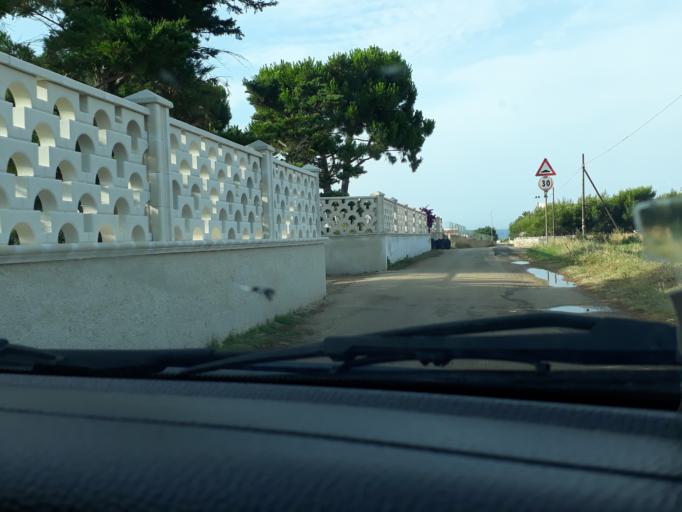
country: IT
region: Apulia
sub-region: Provincia di Brindisi
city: Carovigno
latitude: 40.7608
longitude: 17.6842
